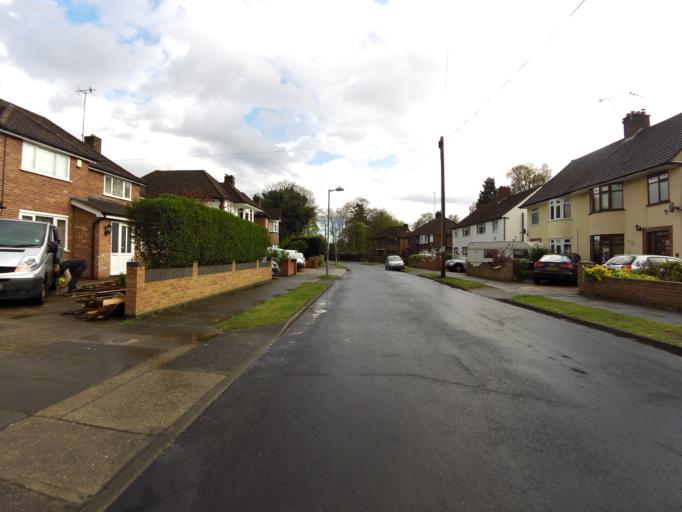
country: GB
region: England
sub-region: Suffolk
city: Kesgrave
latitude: 52.0442
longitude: 1.1978
